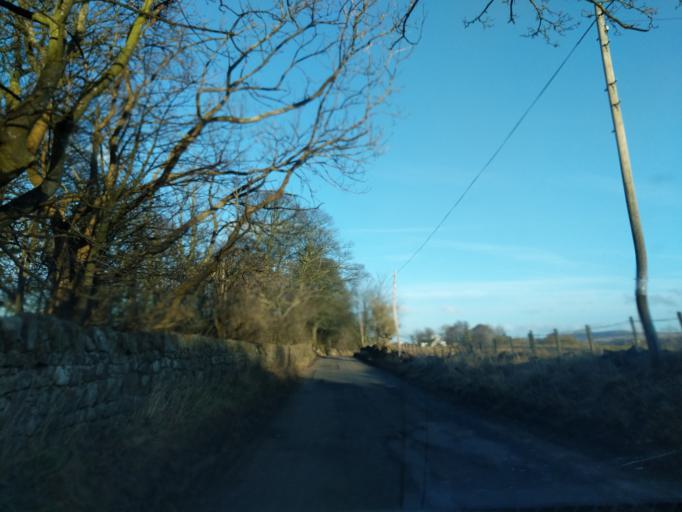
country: GB
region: Scotland
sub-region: Edinburgh
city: Ratho
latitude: 55.8940
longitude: -3.3791
